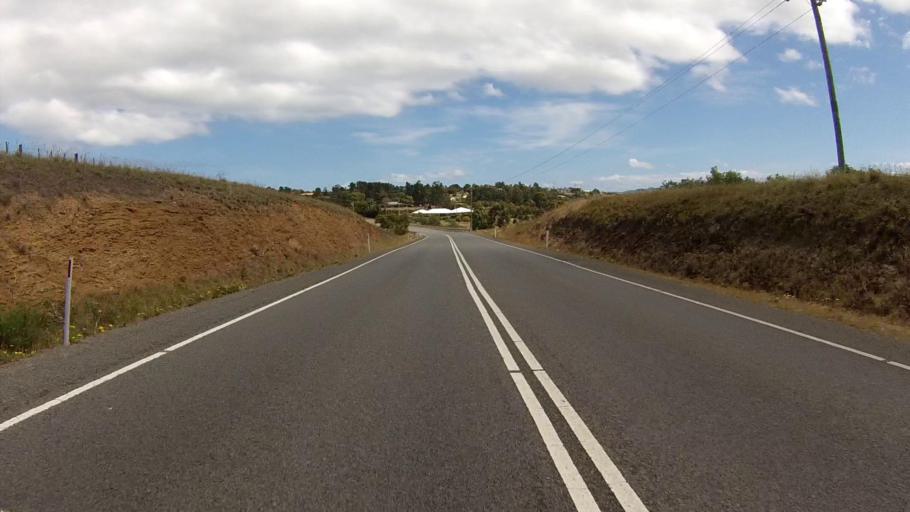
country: AU
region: Tasmania
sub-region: Sorell
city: Sorell
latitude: -42.8103
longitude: 147.6279
